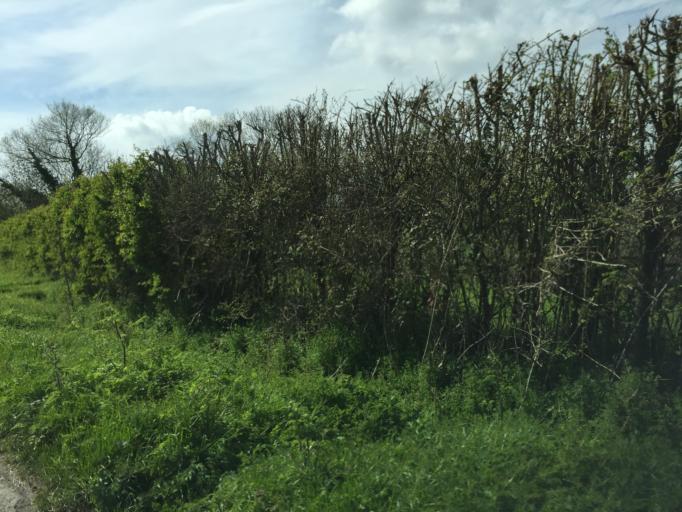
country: GB
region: England
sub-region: South Gloucestershire
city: Severn Beach
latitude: 51.5628
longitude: -2.6210
